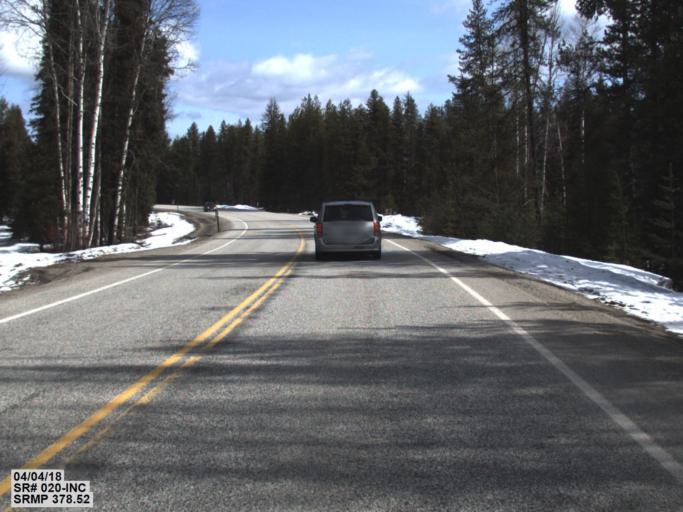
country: US
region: Washington
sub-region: Stevens County
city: Colville
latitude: 48.6032
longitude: -117.5519
